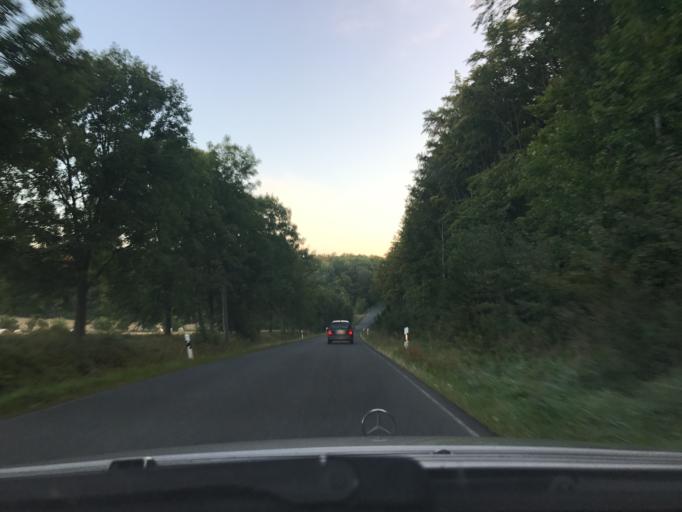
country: DE
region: Thuringia
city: Anrode
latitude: 51.2740
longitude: 10.3552
